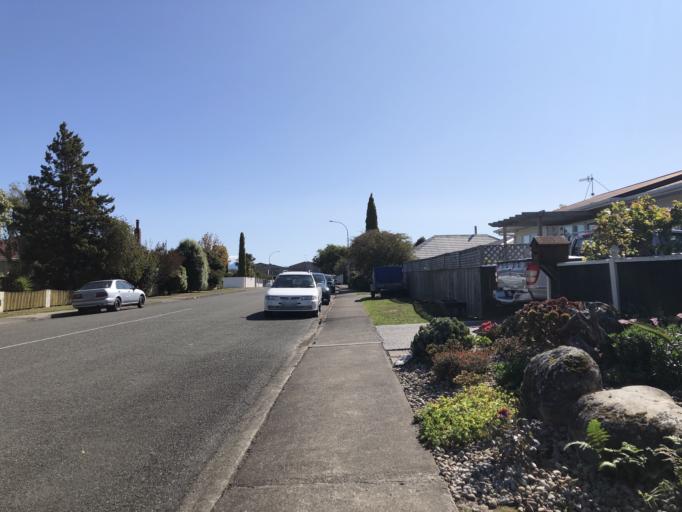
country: NZ
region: Tasman
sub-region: Tasman District
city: Richmond
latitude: -41.3436
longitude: 173.1744
